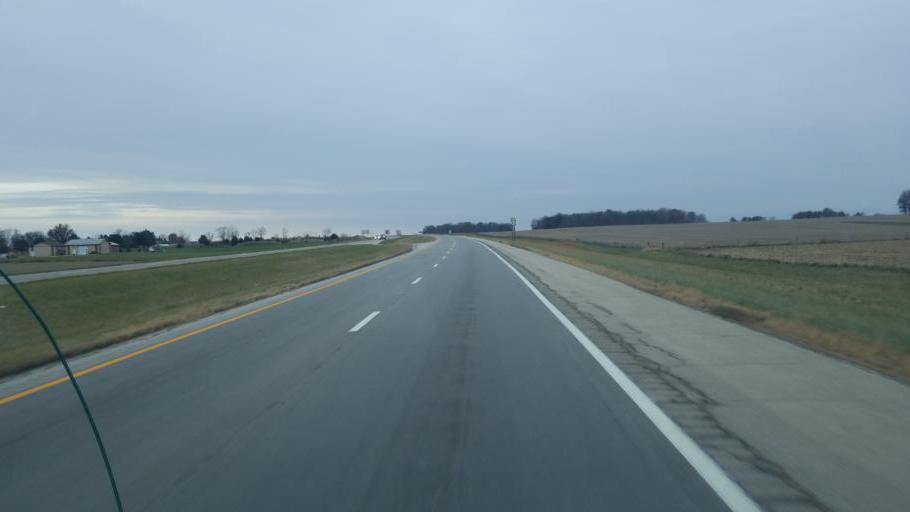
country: US
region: Ohio
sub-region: Auglaize County
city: Wapakoneta
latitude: 40.5658
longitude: -84.2394
